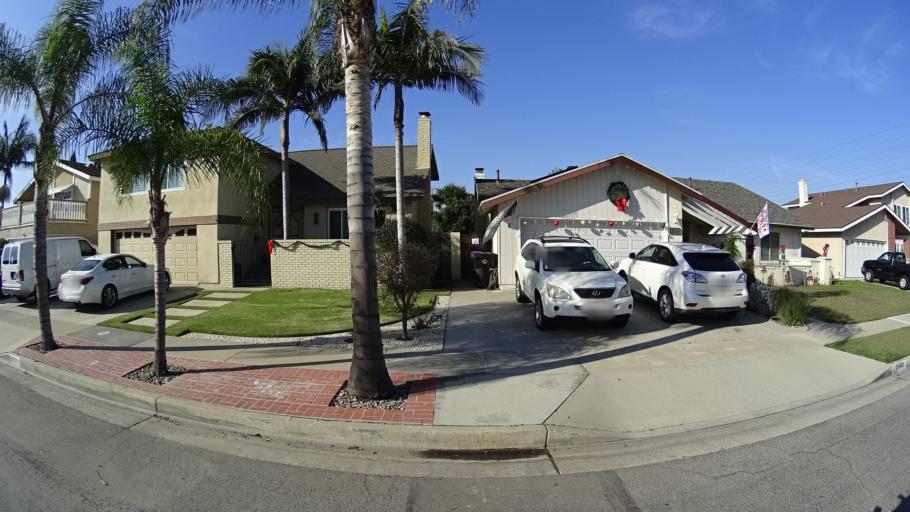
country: US
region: California
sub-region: Orange County
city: Midway City
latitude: 33.7326
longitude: -117.9847
